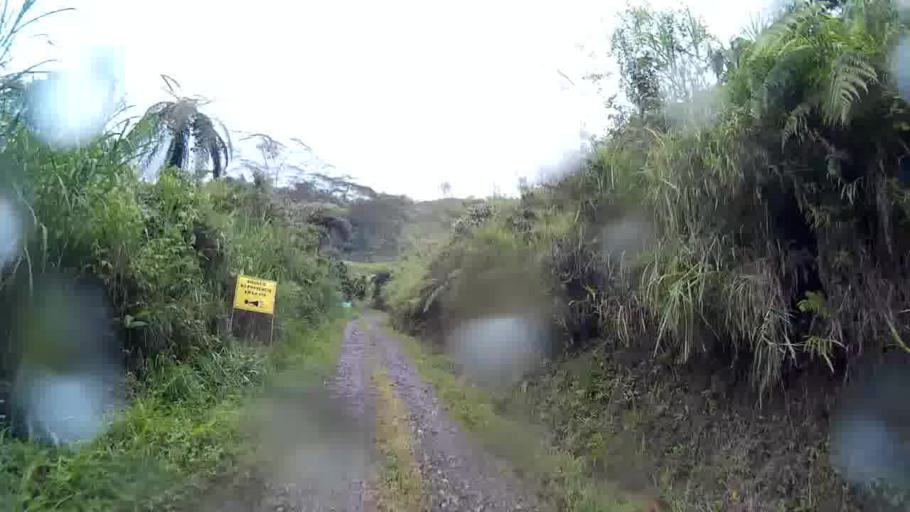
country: CO
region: Quindio
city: Filandia
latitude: 4.7110
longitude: -75.6818
